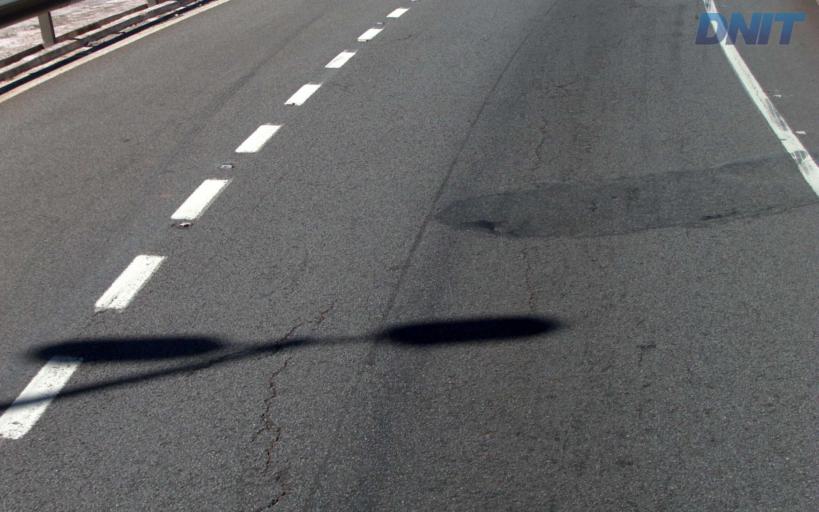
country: BR
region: Minas Gerais
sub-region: Santa Luzia
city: Santa Luzia
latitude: -19.7982
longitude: -43.7551
